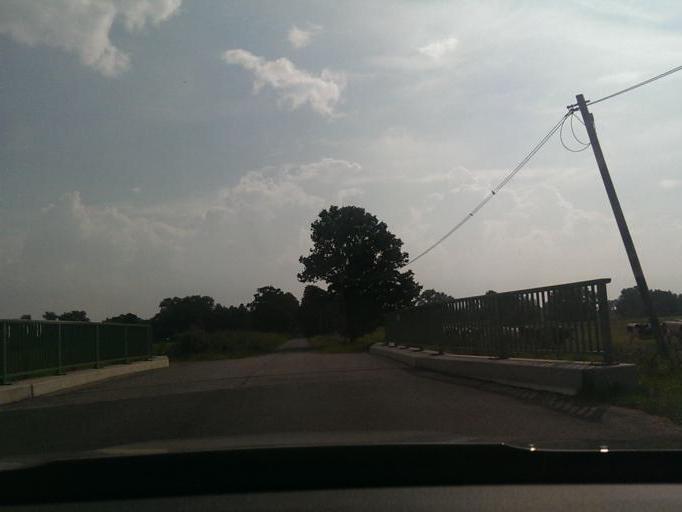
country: DE
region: Lower Saxony
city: Osterholz-Scharmbeck
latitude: 53.1663
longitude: 8.8008
